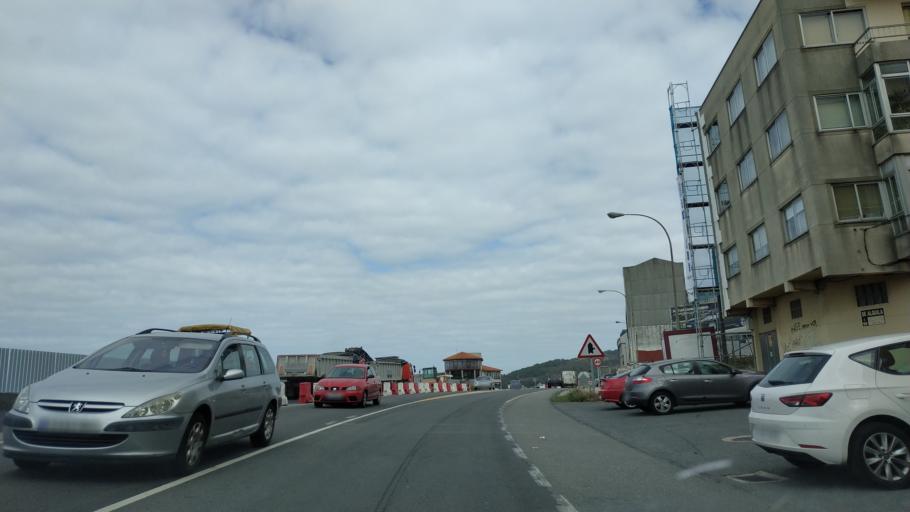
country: ES
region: Galicia
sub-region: Provincia da Coruna
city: Arteixo
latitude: 43.3135
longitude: -8.5011
